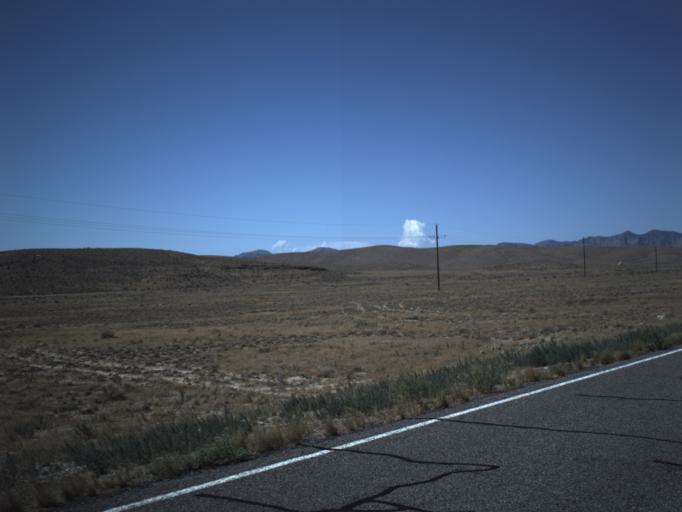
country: US
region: Utah
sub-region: Beaver County
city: Milford
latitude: 39.0388
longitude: -113.3089
